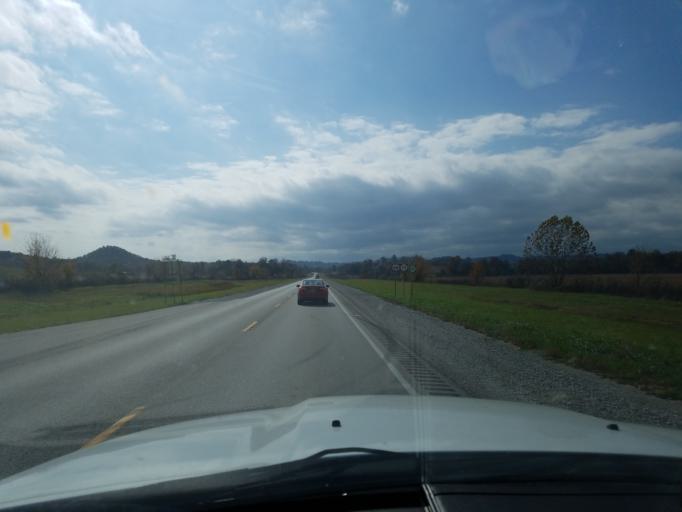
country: US
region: Kentucky
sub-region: Marion County
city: Lebanon
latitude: 37.4973
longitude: -85.2939
